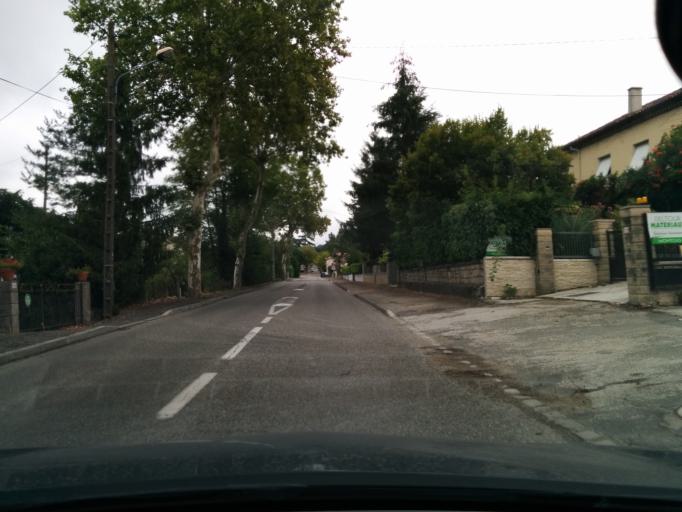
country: FR
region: Midi-Pyrenees
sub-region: Departement du Lot
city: Montcuq
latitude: 44.3377
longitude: 1.1986
